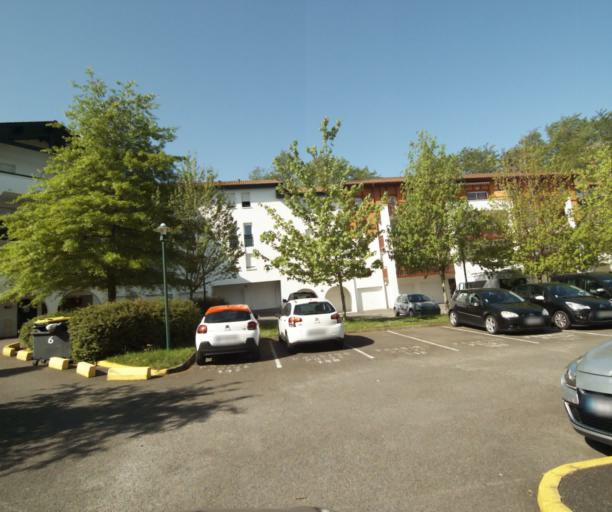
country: FR
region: Aquitaine
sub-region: Departement des Pyrenees-Atlantiques
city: Mouguerre
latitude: 43.4683
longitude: -1.4421
